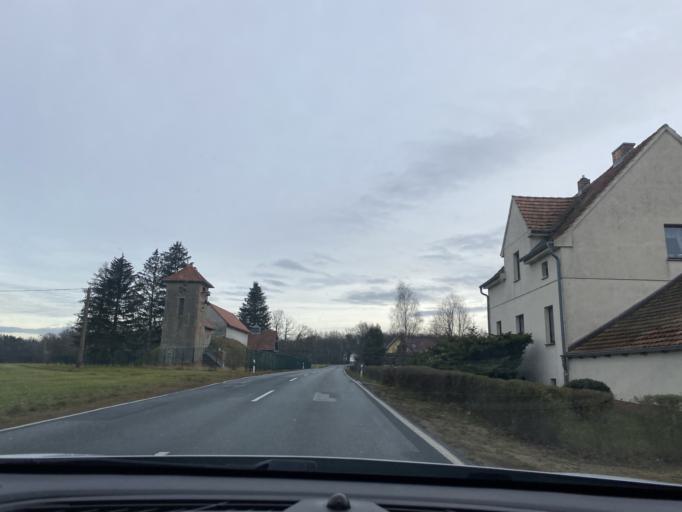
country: DE
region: Saxony
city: Reichenbach
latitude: 51.1268
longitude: 14.8133
